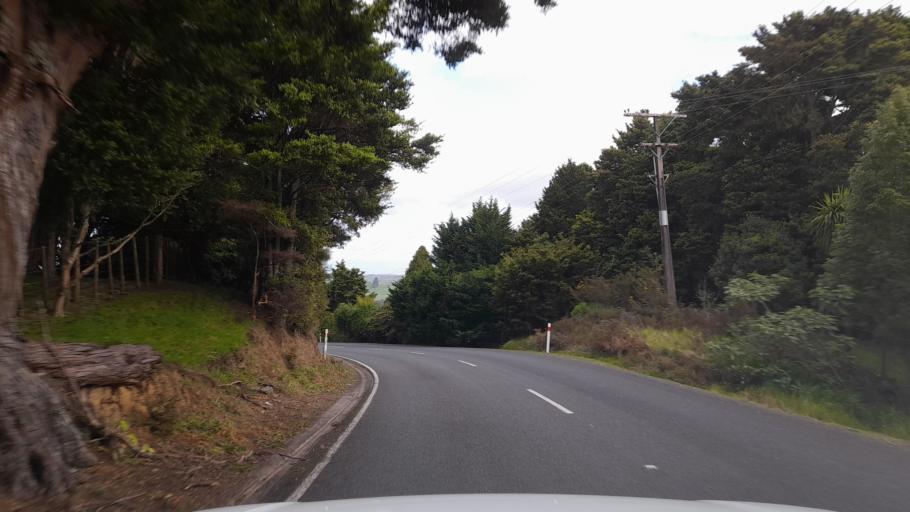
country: NZ
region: Northland
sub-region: Whangarei
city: Maungatapere
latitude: -35.7585
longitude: 174.2361
